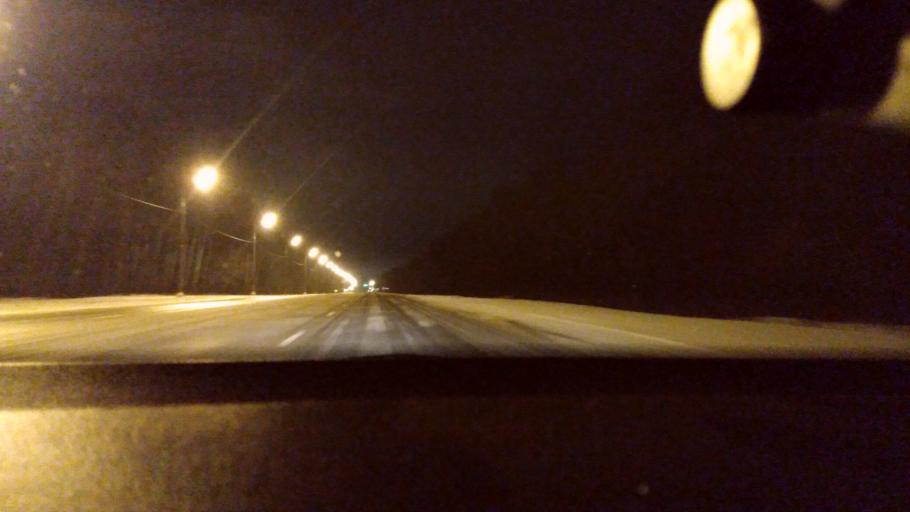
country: RU
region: Moskovskaya
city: Beloozerskiy
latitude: 55.3788
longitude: 38.3706
